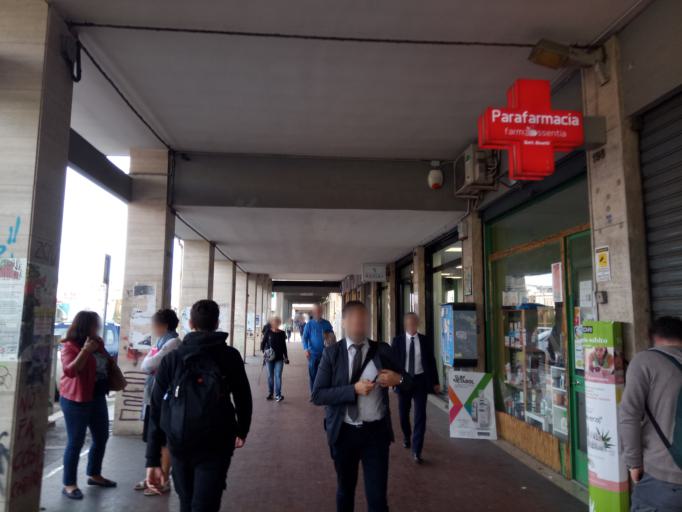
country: IT
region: Apulia
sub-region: Provincia di Bari
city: Bari
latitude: 41.1169
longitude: 16.8689
